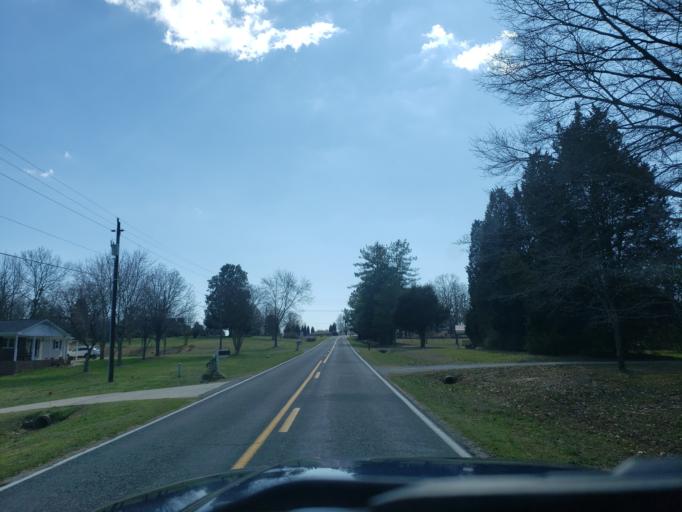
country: US
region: North Carolina
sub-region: Cleveland County
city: White Plains
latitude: 35.2203
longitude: -81.4078
